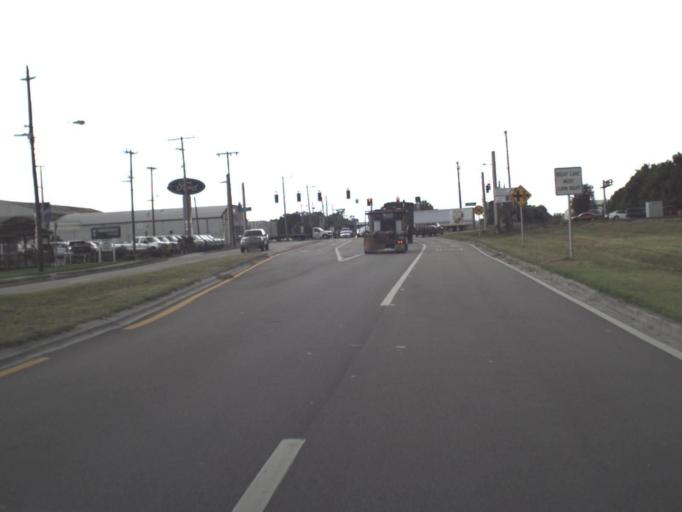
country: US
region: Florida
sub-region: Hillsborough County
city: Plant City
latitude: 28.0184
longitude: -82.1066
